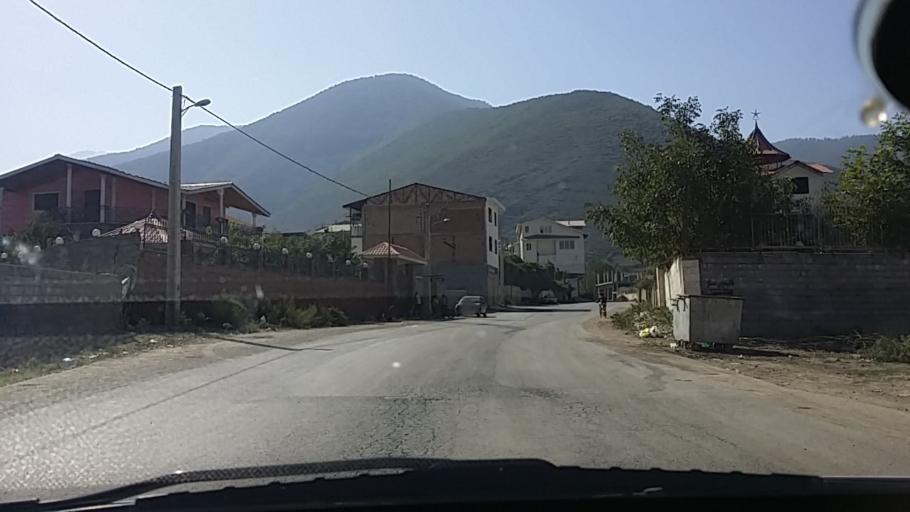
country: IR
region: Mazandaran
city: `Abbasabad
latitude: 36.4989
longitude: 51.1522
